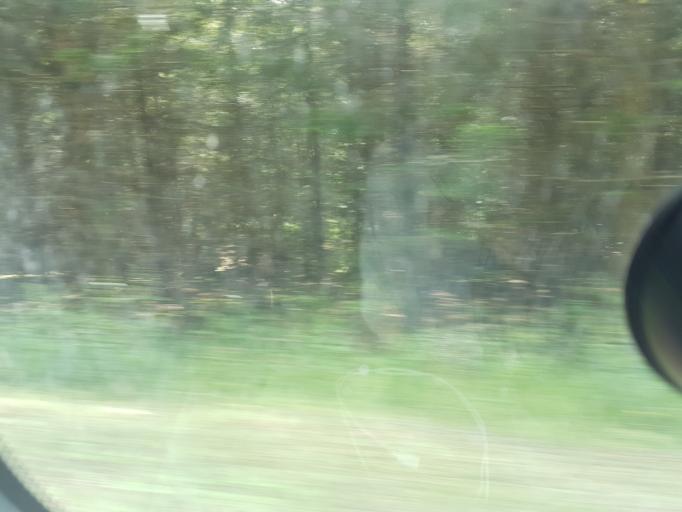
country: FR
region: Bourgogne
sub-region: Departement de la Cote-d'Or
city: Saulieu
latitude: 47.1732
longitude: 4.1229
